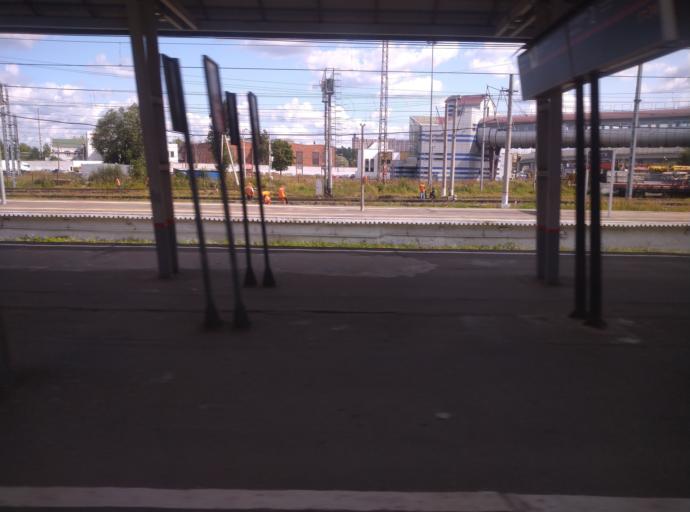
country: RU
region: St.-Petersburg
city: Obukhovo
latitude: 59.8481
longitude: 30.4551
